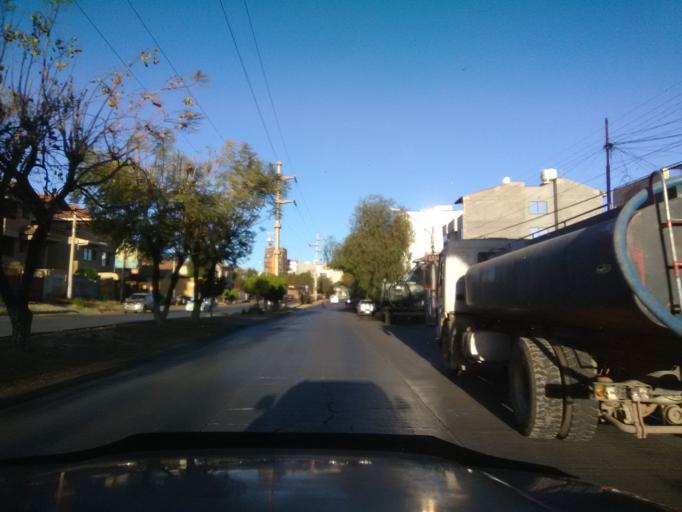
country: BO
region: Cochabamba
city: Cochabamba
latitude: -17.3655
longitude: -66.1596
